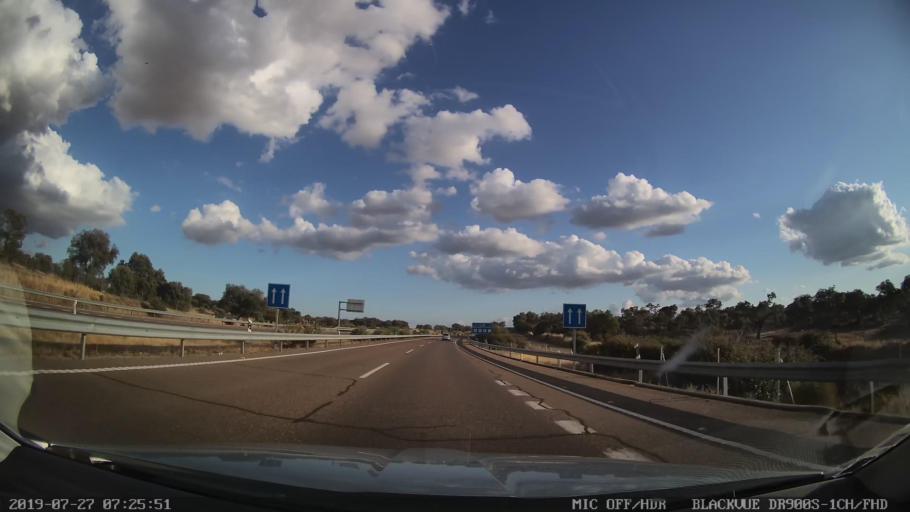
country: ES
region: Extremadura
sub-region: Provincia de Caceres
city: Villamesias
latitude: 39.2688
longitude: -5.8570
